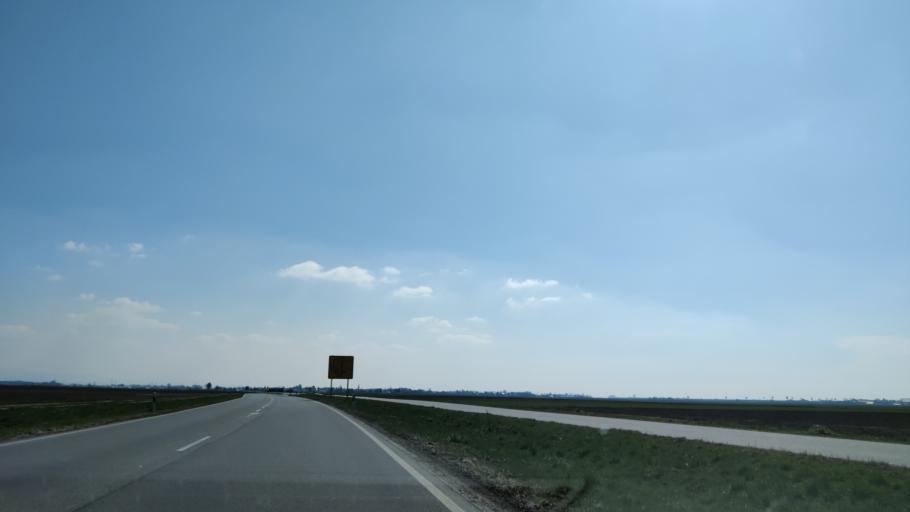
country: DE
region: Bavaria
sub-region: Lower Bavaria
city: Strasskirchen
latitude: 48.8409
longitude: 12.6797
